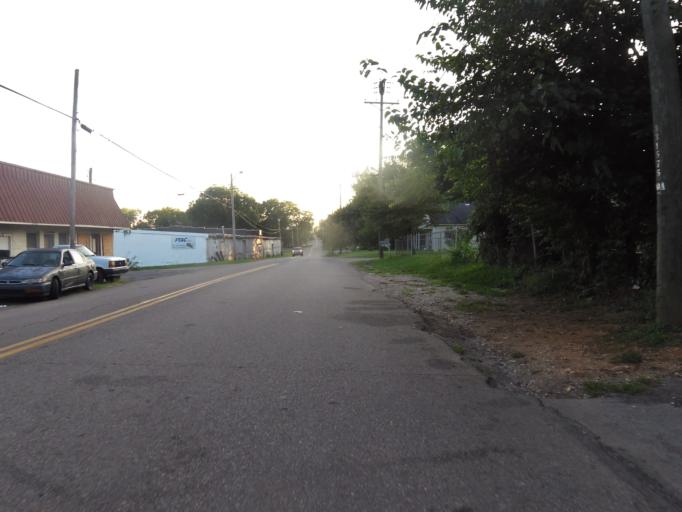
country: US
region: Tennessee
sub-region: Knox County
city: Knoxville
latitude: 35.9938
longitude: -83.9082
